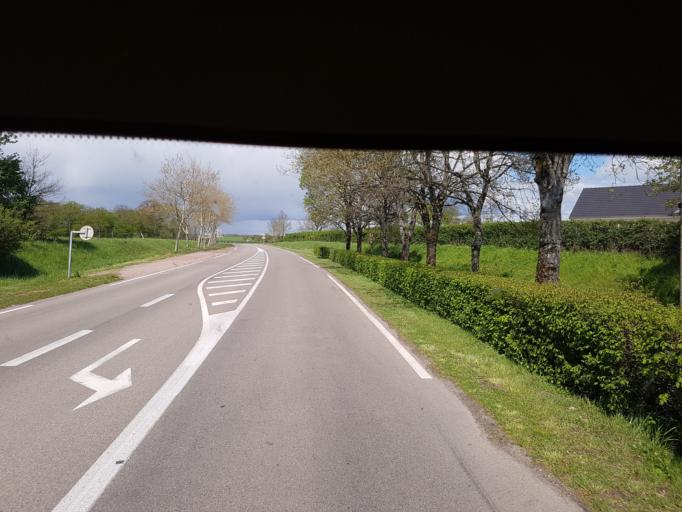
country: FR
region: Bourgogne
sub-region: Departement de Saone-et-Loire
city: Etang-sur-Arroux
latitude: 46.8724
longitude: 4.1761
